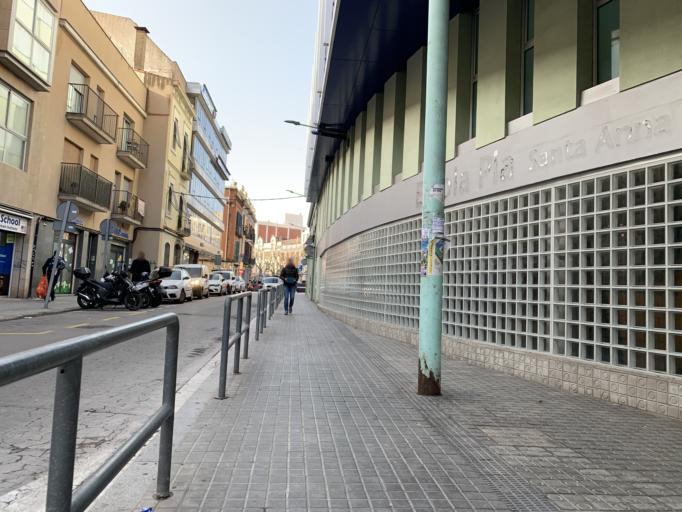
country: ES
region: Catalonia
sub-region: Provincia de Barcelona
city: Mataro
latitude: 41.5375
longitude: 2.4451
